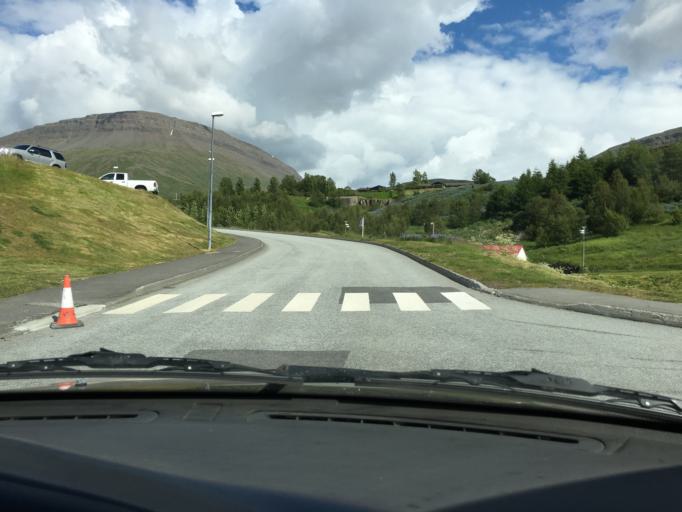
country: IS
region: East
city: Reydarfjoerdur
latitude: 65.0331
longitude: -14.2055
